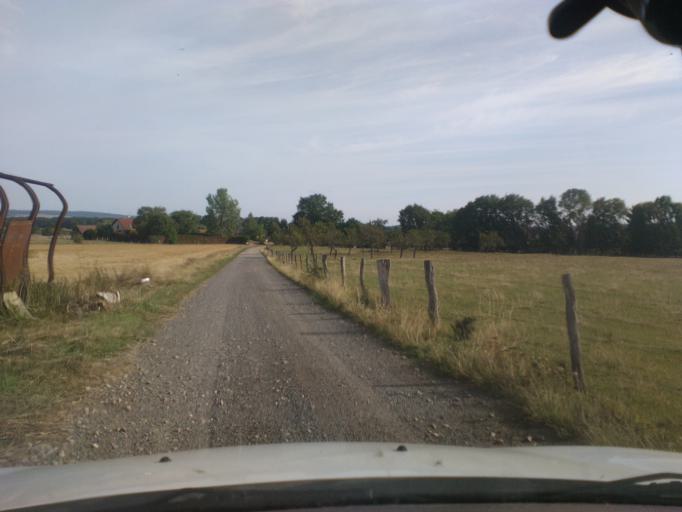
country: FR
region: Lorraine
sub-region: Departement des Vosges
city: Mirecourt
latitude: 48.3295
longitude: 6.0951
